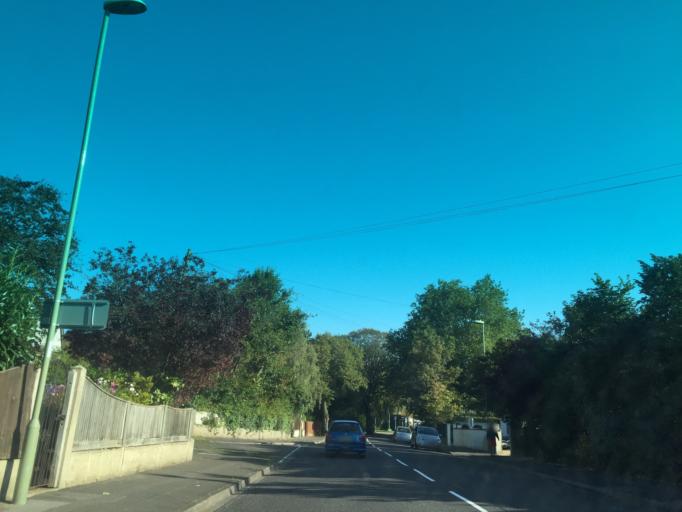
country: GB
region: England
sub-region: Hampshire
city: Gosport
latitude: 50.7898
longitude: -1.1434
